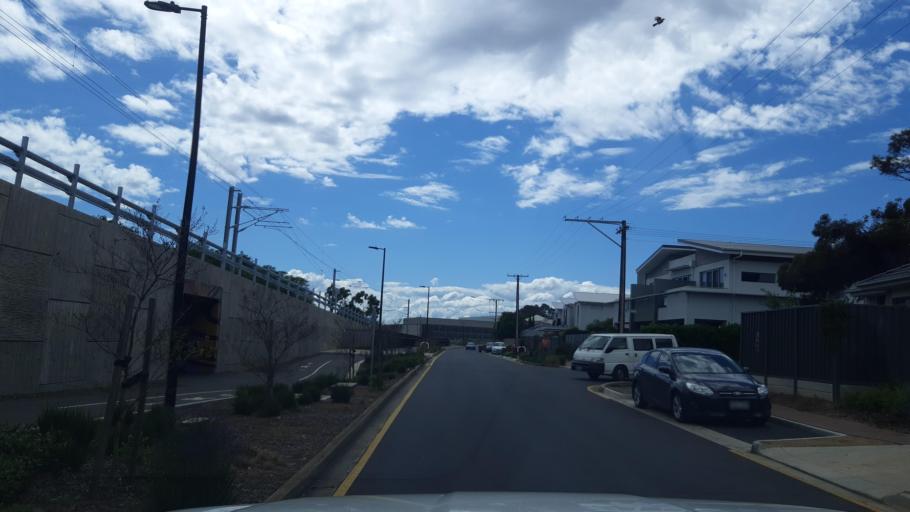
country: AU
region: South Australia
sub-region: Marion
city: Marion
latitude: -35.0157
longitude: 138.5660
